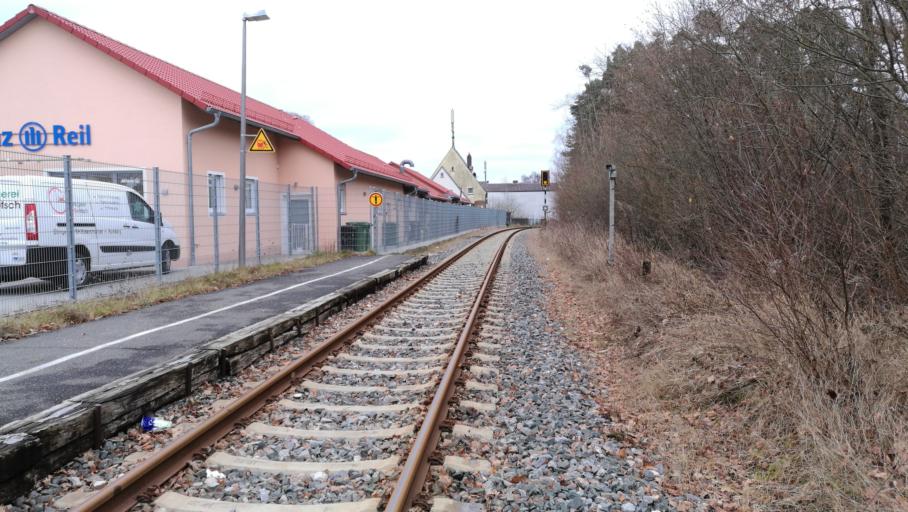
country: DE
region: Bavaria
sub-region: Regierungsbezirk Mittelfranken
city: Roth
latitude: 49.2154
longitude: 11.1384
